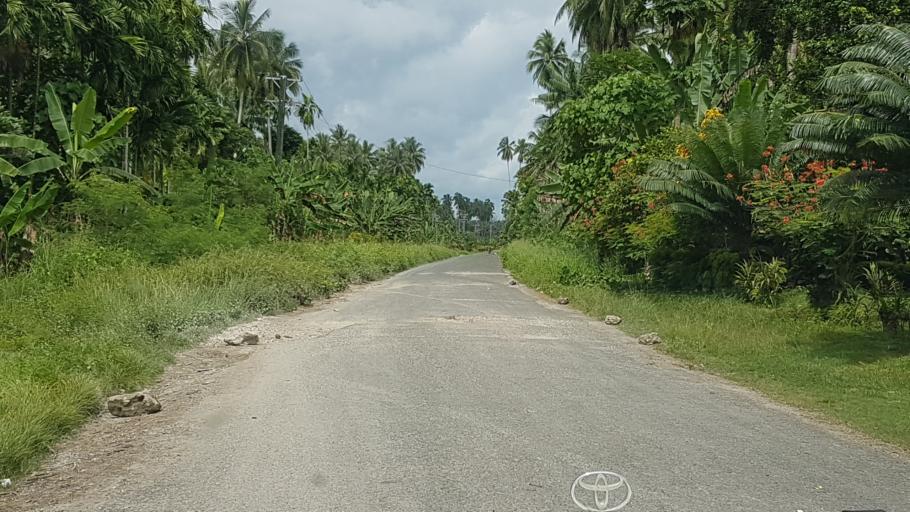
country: PG
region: Madang
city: Madang
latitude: -4.8153
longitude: 145.7672
